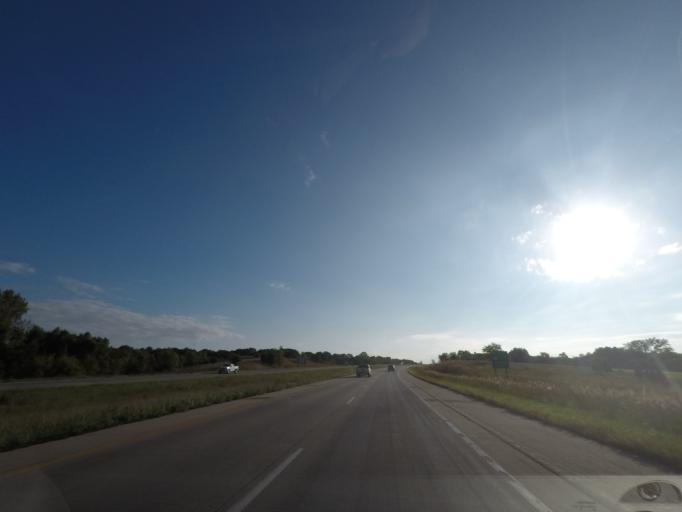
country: US
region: Iowa
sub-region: Warren County
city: Carlisle
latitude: 41.5109
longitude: -93.5536
